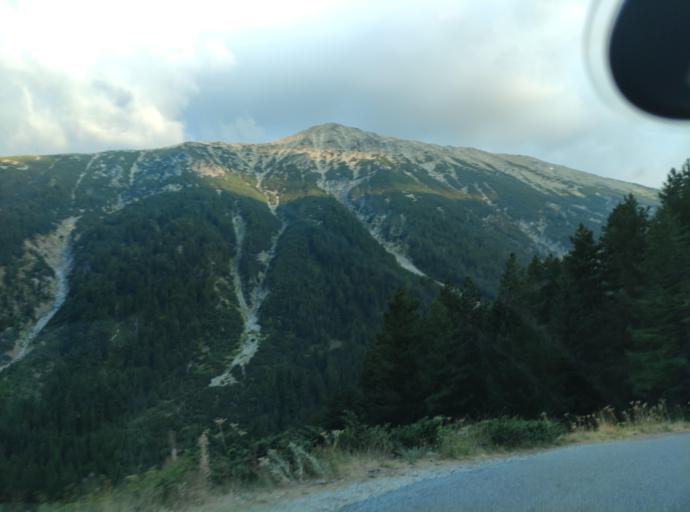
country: BG
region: Blagoevgrad
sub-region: Obshtina Bansko
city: Bansko
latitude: 41.7659
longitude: 23.4208
